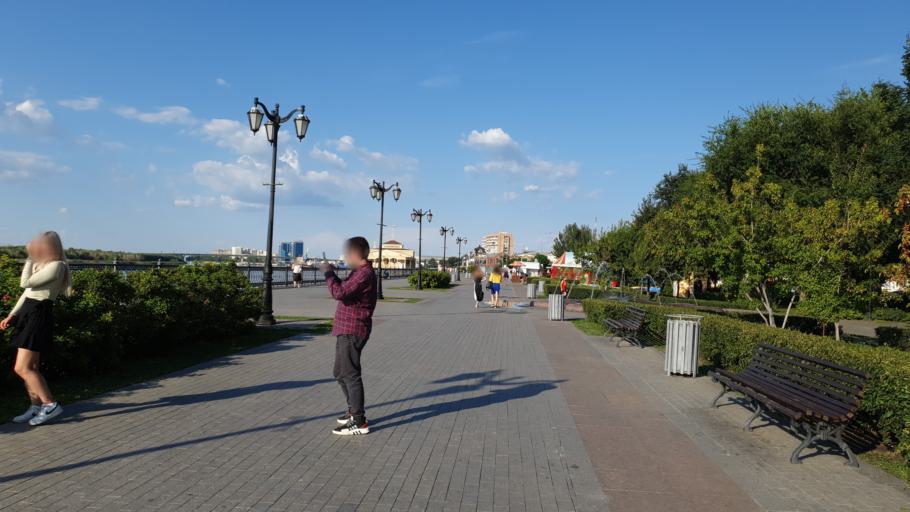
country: RU
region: Astrakhan
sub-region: Gorod Astrakhan'
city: Astrakhan'
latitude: 46.3509
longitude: 48.0237
